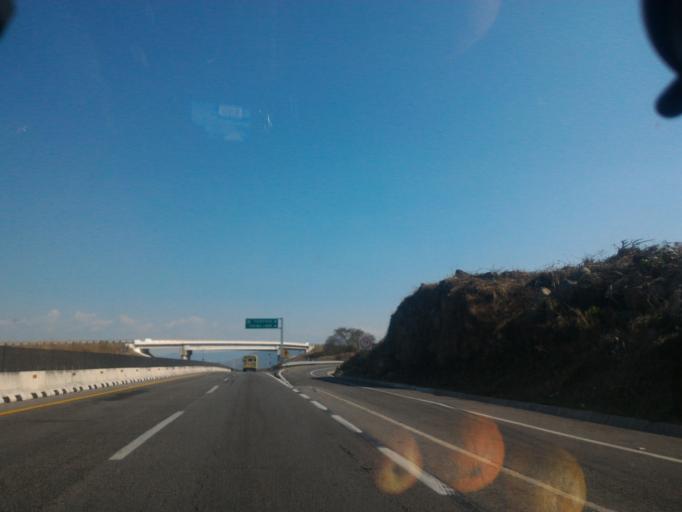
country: MX
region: Jalisco
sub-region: Zapotlan el Grande
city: Ciudad Guzman [CERESO]
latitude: 19.6441
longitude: -103.4721
